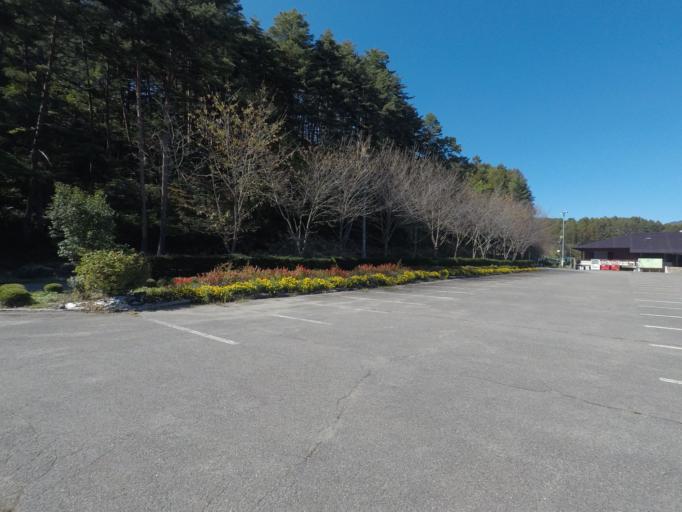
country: JP
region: Nagano
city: Ina
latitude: 35.9675
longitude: 137.7470
